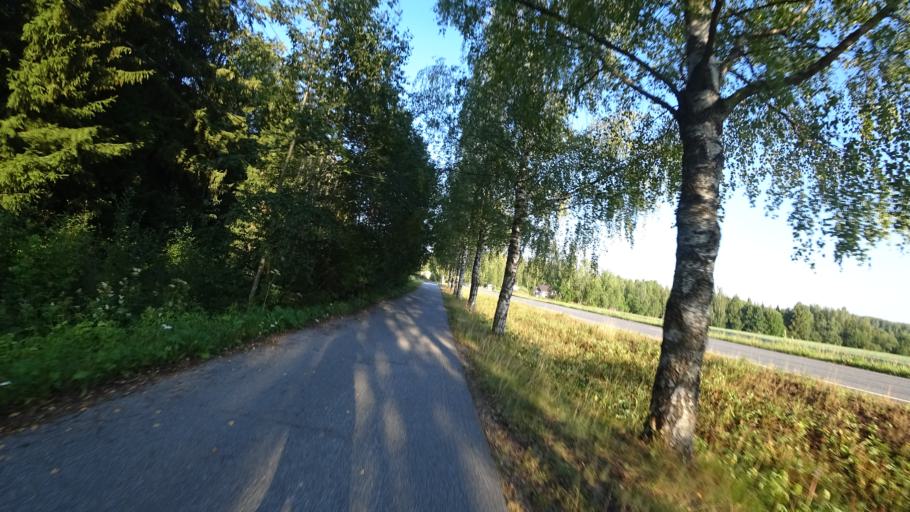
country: FI
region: Pirkanmaa
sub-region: Tampere
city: Nokia
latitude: 61.4703
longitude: 23.3911
